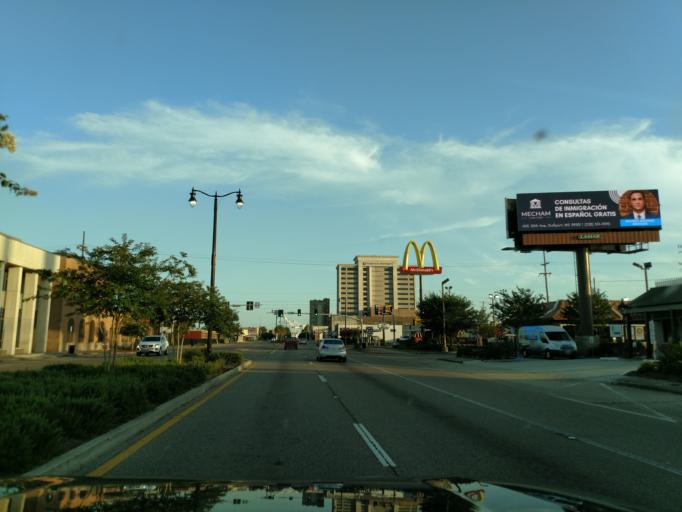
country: US
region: Mississippi
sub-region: Harrison County
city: Gulfport
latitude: 30.3722
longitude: -89.0930
